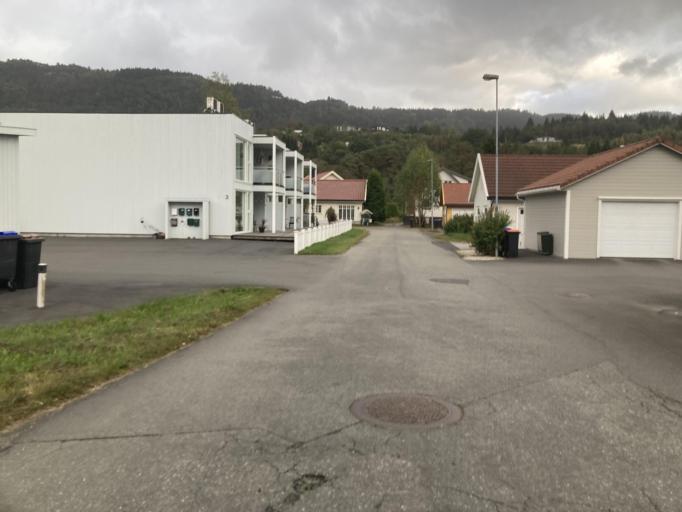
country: NO
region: Vest-Agder
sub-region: Kvinesdal
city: Liknes
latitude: 58.3220
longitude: 6.9682
